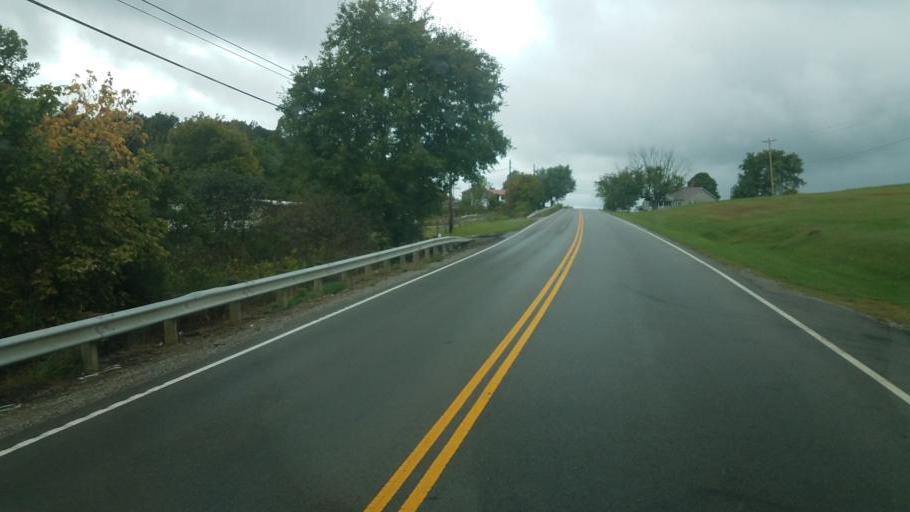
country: US
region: Ohio
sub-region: Scioto County
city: Wheelersburg
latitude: 38.7779
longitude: -82.7780
